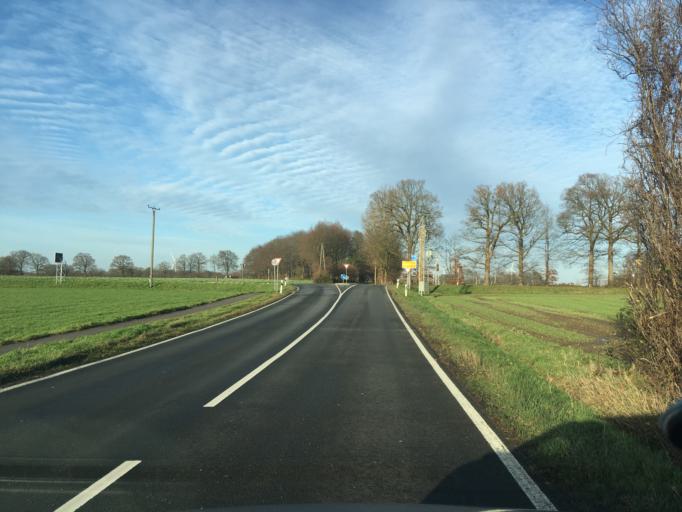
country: DE
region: North Rhine-Westphalia
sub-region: Regierungsbezirk Munster
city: Gescher
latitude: 51.9655
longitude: 7.0621
